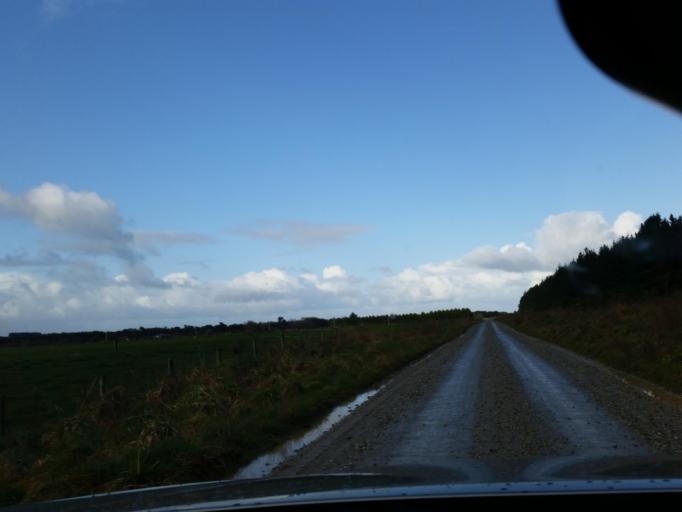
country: NZ
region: Southland
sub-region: Southland District
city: Winton
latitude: -46.2342
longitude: 168.4837
